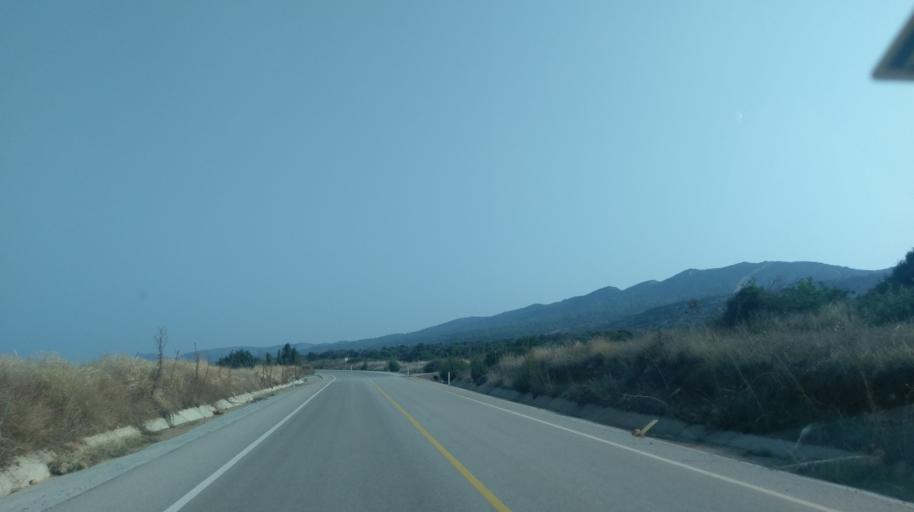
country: CY
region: Ammochostos
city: Leonarisso
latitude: 35.4439
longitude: 33.9696
